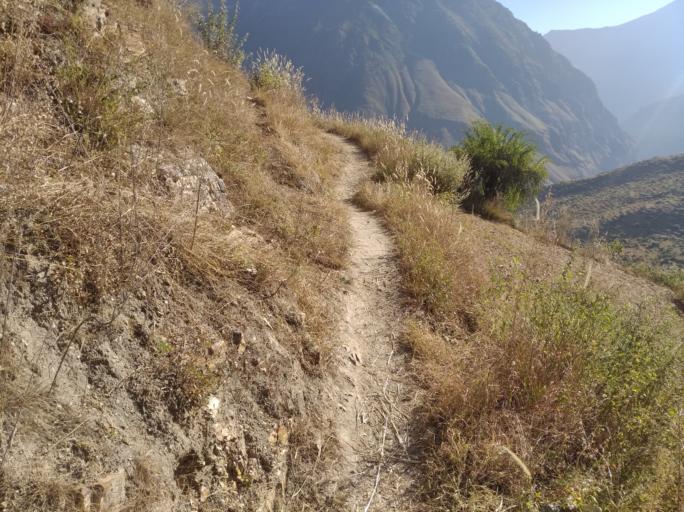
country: NP
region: Western Region
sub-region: Dhawalagiri Zone
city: Jomsom
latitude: 28.8846
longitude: 82.9695
